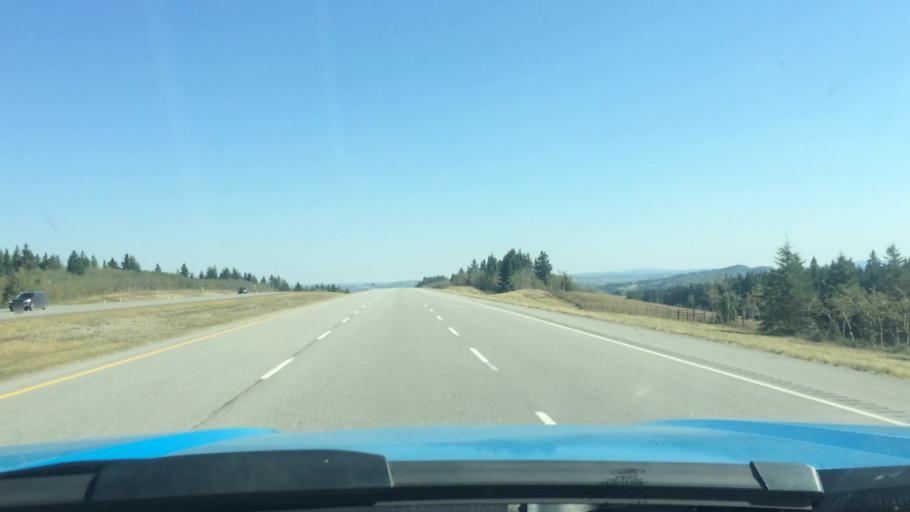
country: CA
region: Alberta
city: Cochrane
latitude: 51.1434
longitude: -114.7253
